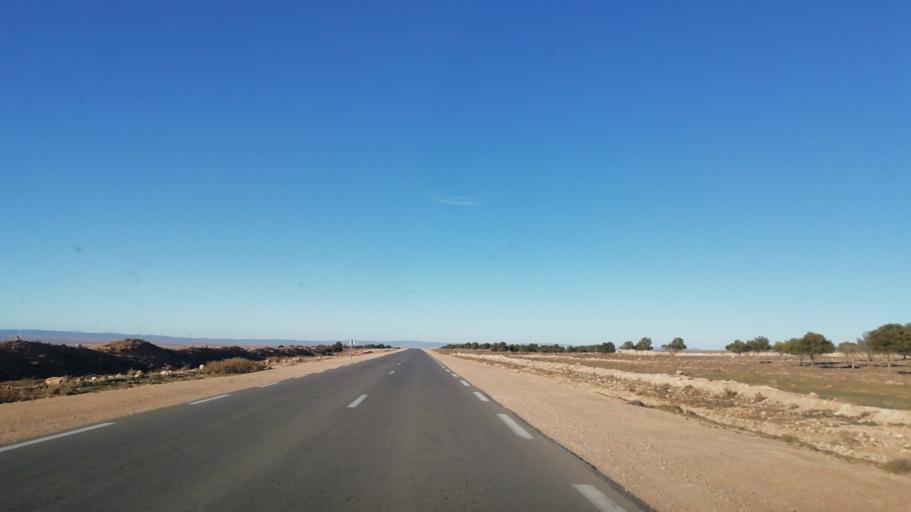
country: DZ
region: Tlemcen
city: Sebdou
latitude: 34.2803
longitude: -1.2591
